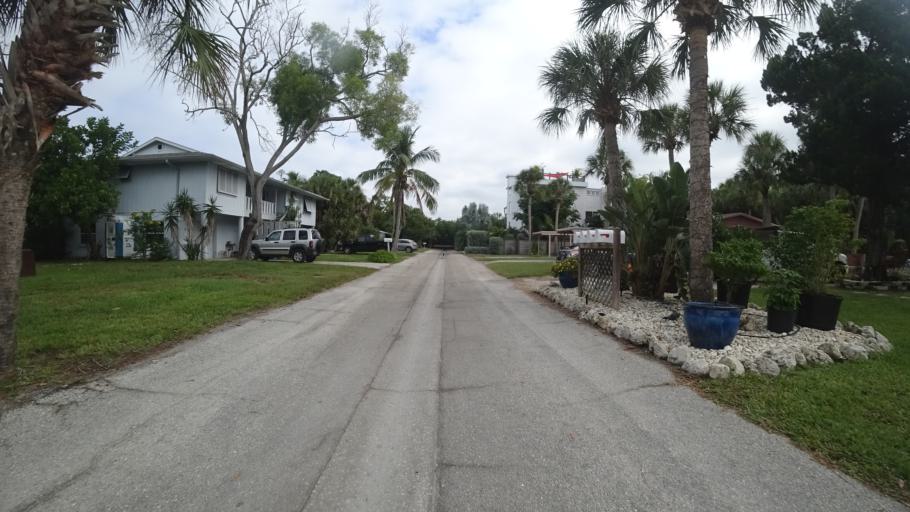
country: US
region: Florida
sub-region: Manatee County
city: Longboat Key
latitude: 27.4145
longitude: -82.6566
